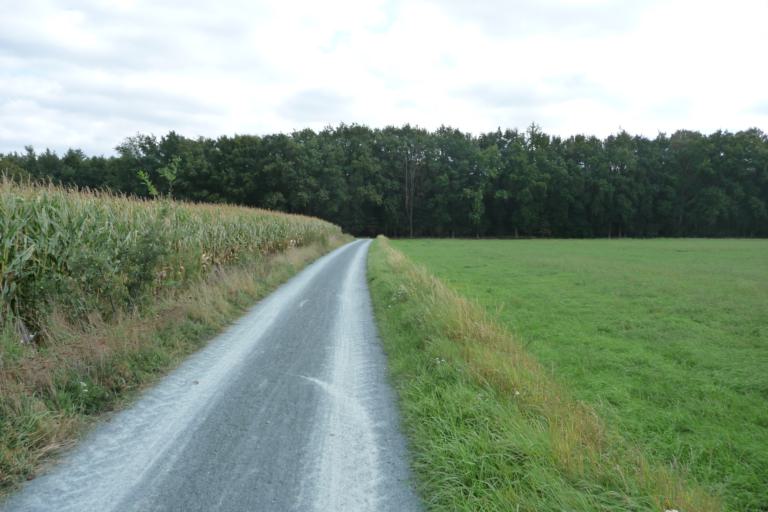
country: BE
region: Flanders
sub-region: Provincie Antwerpen
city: Wuustwezel
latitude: 51.3768
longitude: 4.5805
